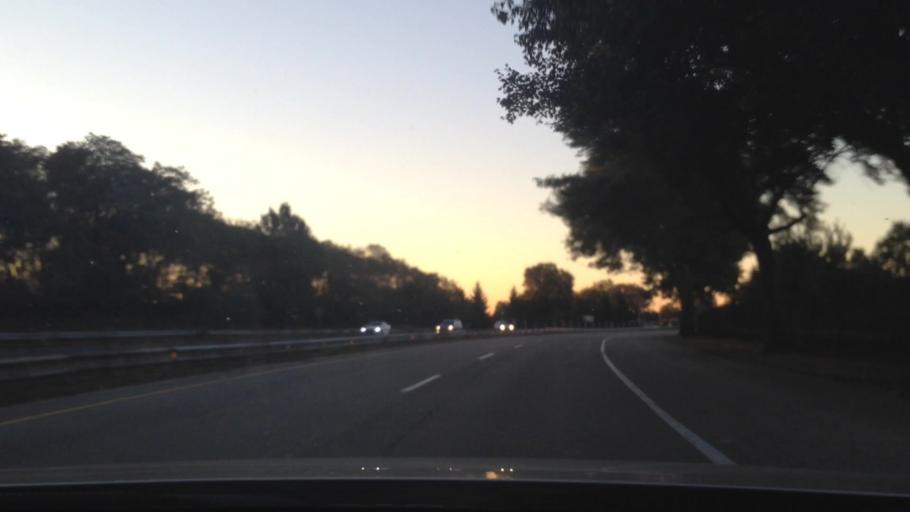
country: US
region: New York
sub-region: Suffolk County
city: Mount Sinai
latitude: 40.9357
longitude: -73.0096
